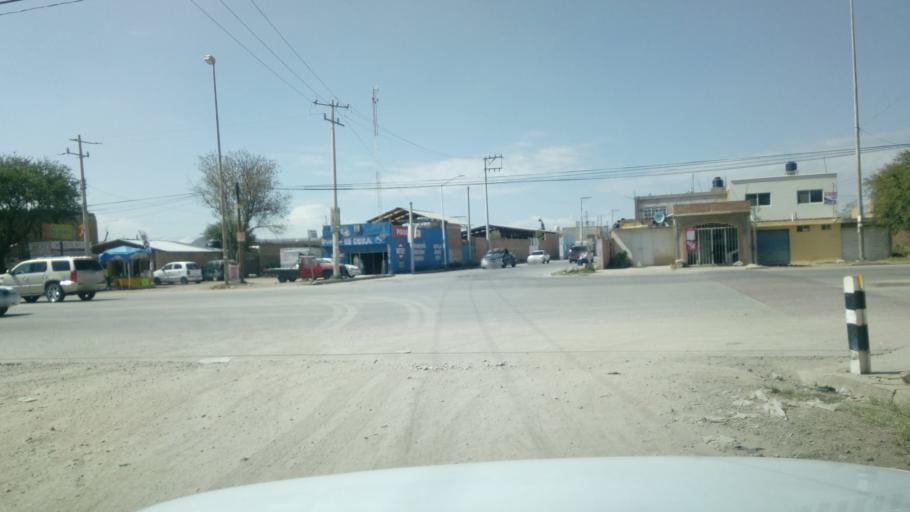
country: MX
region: Durango
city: Victoria de Durango
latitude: 23.9901
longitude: -104.6882
